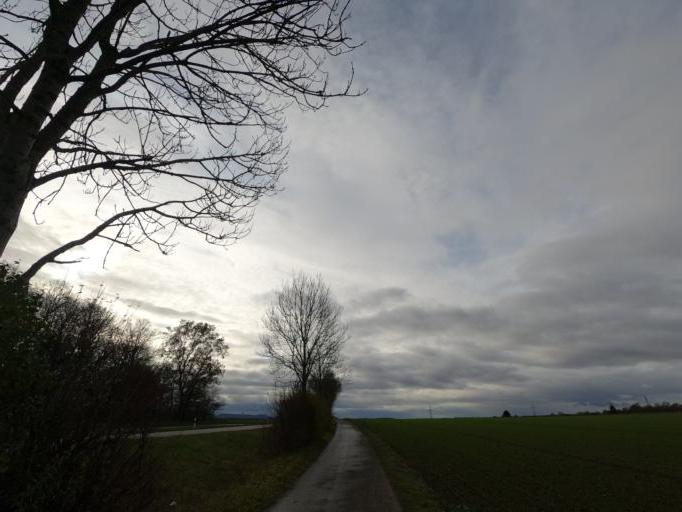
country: DE
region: Baden-Wuerttemberg
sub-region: Regierungsbezirk Stuttgart
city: Schlierbach
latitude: 48.6833
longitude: 9.5401
